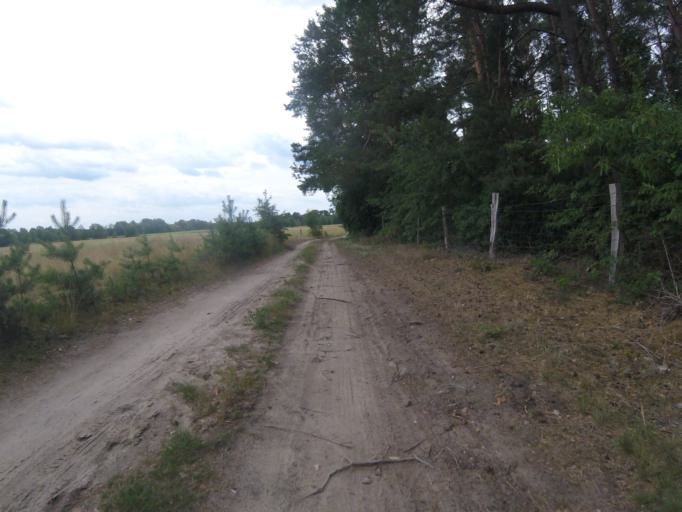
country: DE
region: Brandenburg
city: Bestensee
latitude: 52.2567
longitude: 13.6996
